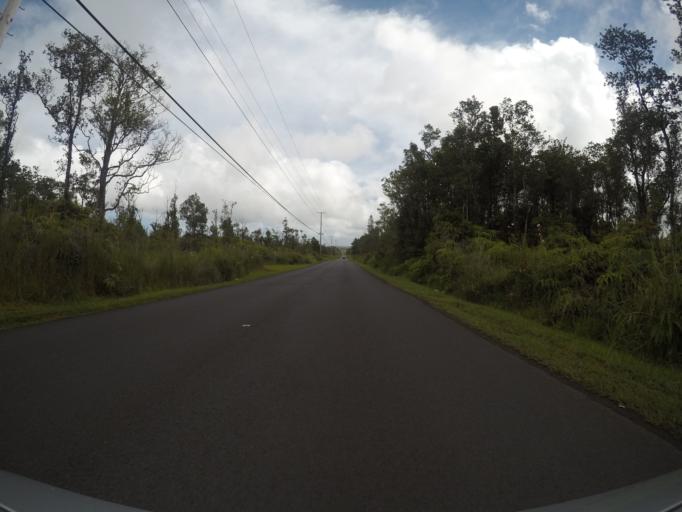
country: US
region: Hawaii
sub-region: Hawaii County
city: Fern Acres
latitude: 19.4718
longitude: -155.1381
